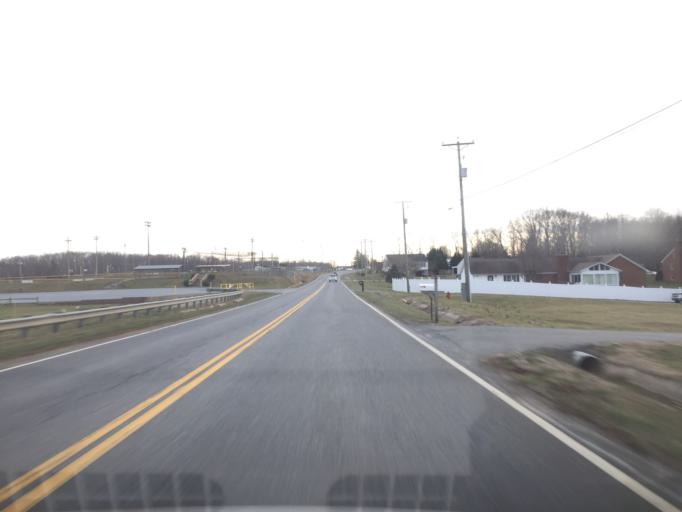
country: US
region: Virginia
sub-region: Bedford County
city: Forest
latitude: 37.3364
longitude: -79.2870
